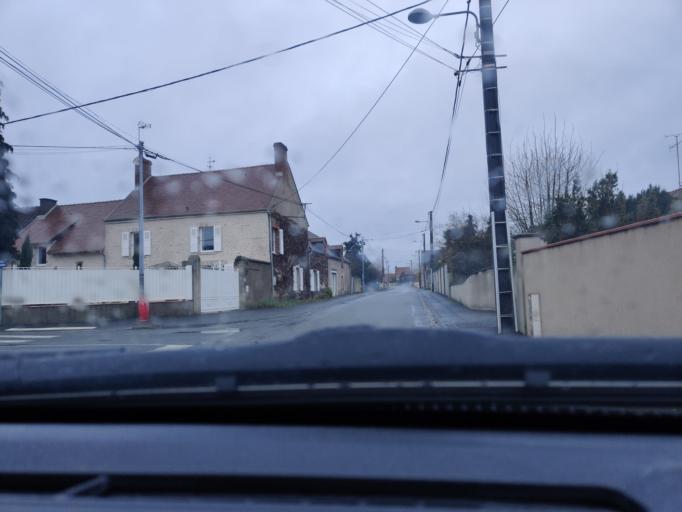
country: FR
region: Centre
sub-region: Departement du Loiret
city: La Chapelle-Saint-Mesmin
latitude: 47.8933
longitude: 1.8251
